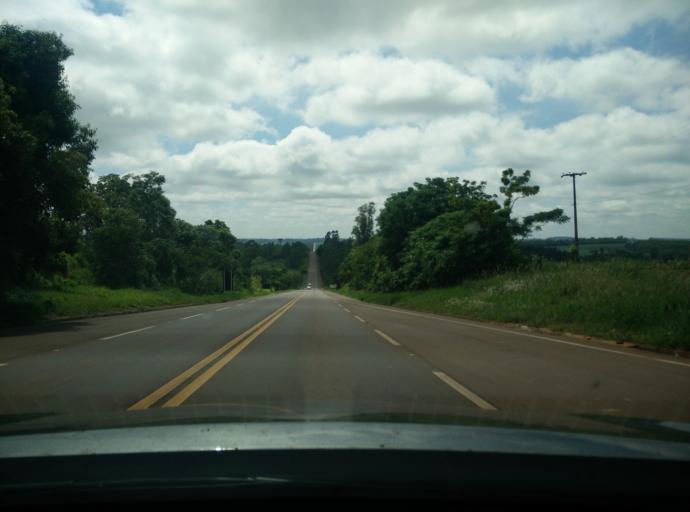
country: BR
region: Parana
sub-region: Campo Mourao
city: Campo Mourao
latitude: -23.9736
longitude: -52.5545
